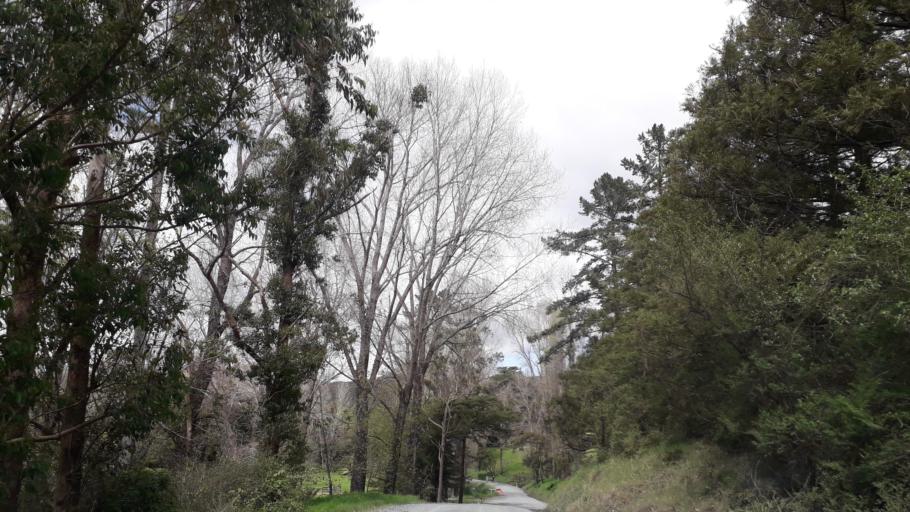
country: NZ
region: Northland
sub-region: Far North District
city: Taipa
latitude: -35.0909
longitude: 173.5148
